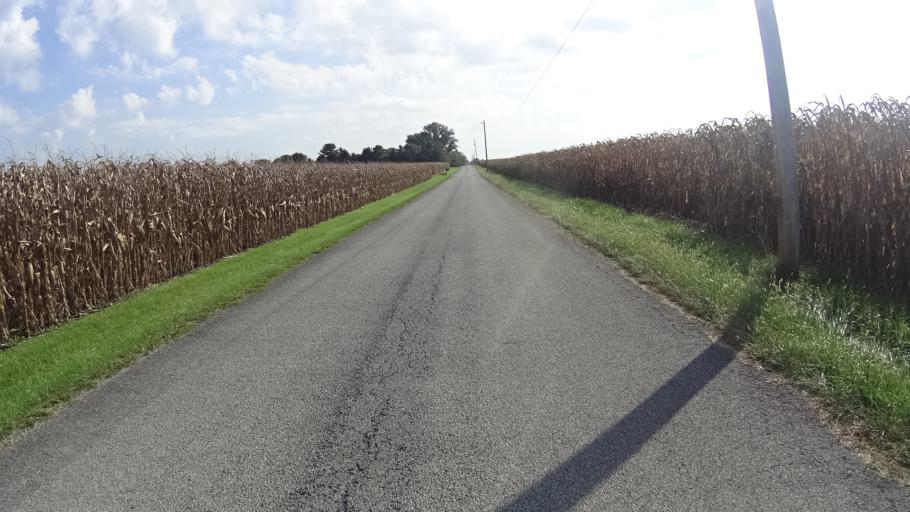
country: US
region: Indiana
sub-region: Madison County
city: Lapel
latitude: 40.0096
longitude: -85.8610
